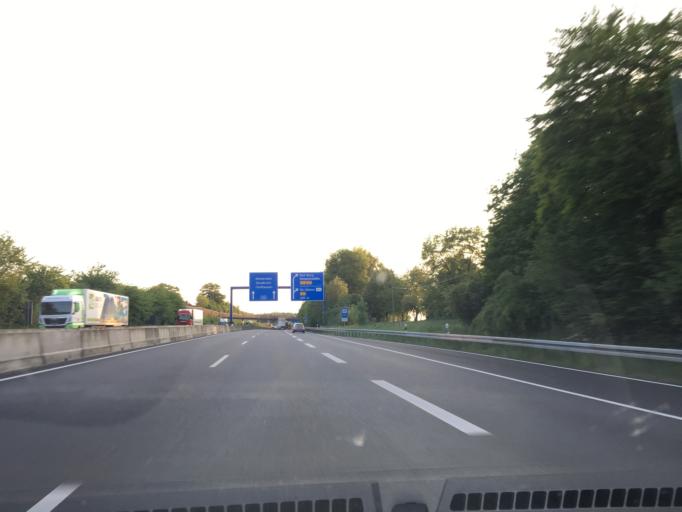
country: DE
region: Lower Saxony
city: Osnabrueck
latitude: 52.2463
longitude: 8.0733
